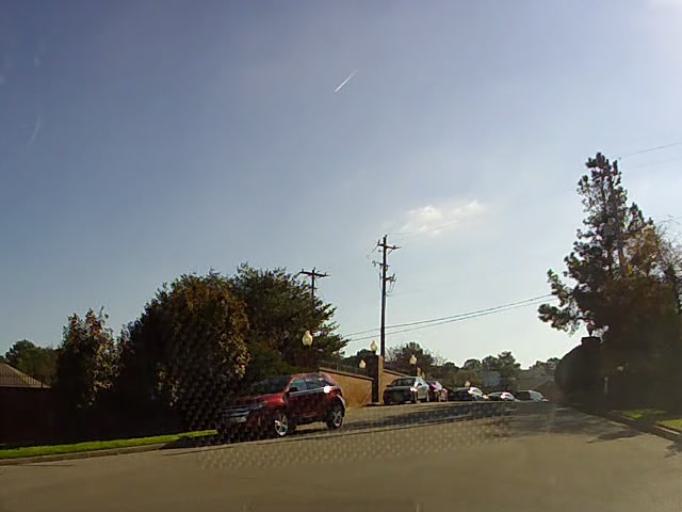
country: US
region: Tennessee
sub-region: Shelby County
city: Germantown
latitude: 35.0559
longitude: -89.8493
